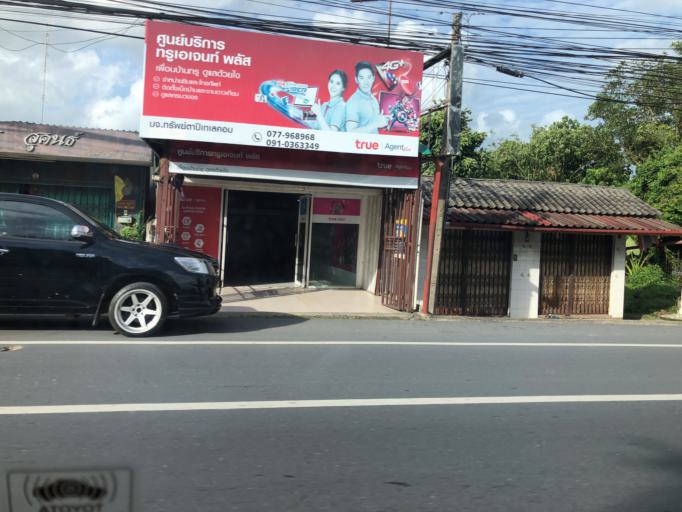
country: TH
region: Phuket
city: Thalang
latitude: 7.9896
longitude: 98.3557
